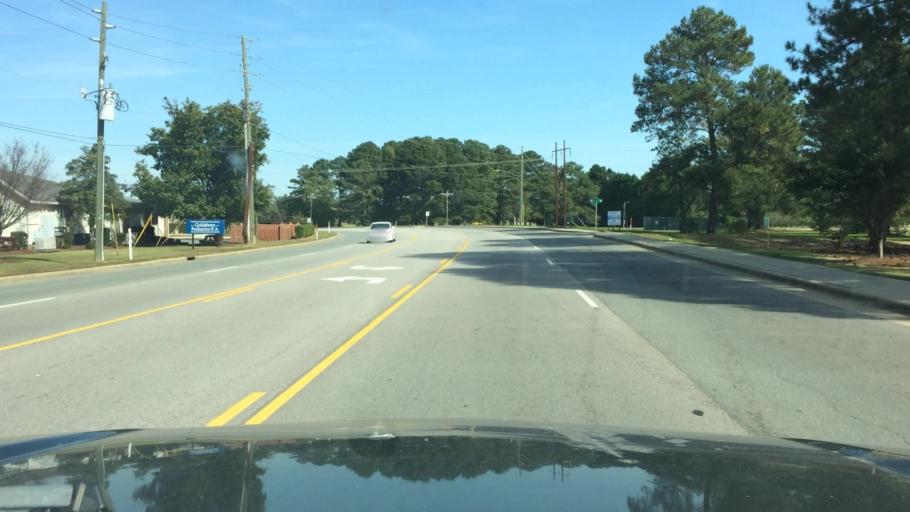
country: US
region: North Carolina
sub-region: Wayne County
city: Goldsboro
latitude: 35.4013
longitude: -77.9517
